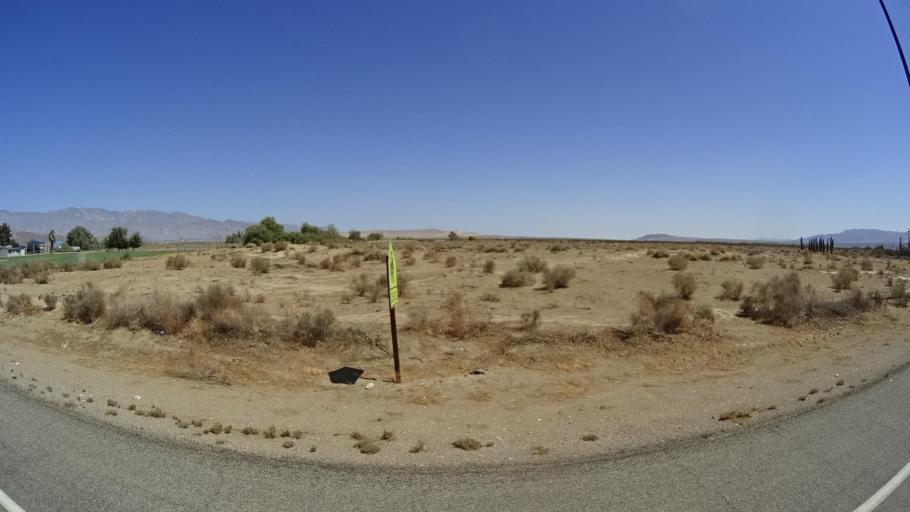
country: US
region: California
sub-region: San Diego County
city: Borrego Springs
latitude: 33.2542
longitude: -116.3479
